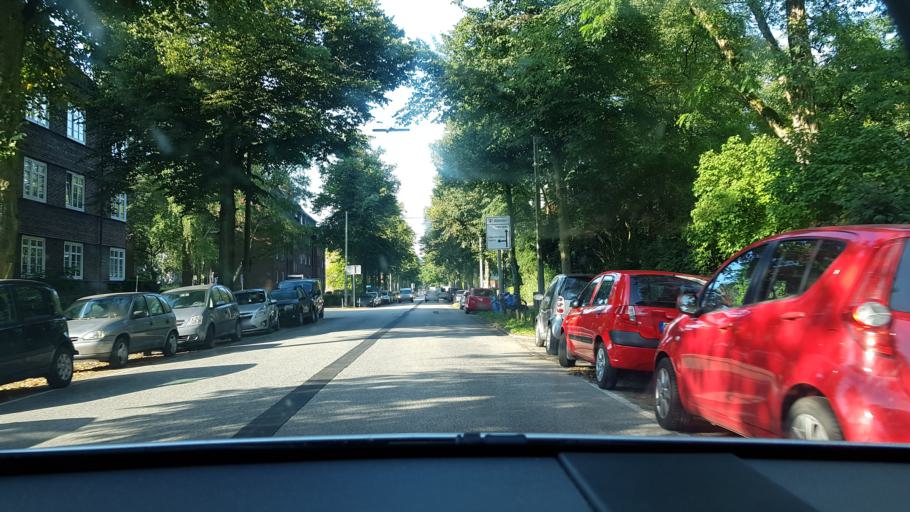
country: DE
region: Hamburg
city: Ohlsdorf
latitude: 53.6161
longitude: 10.0243
